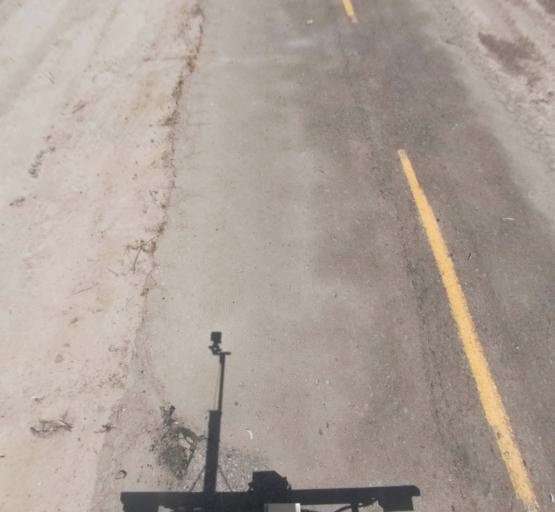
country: US
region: California
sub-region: Fresno County
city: Kerman
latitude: 36.8294
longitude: -120.1616
